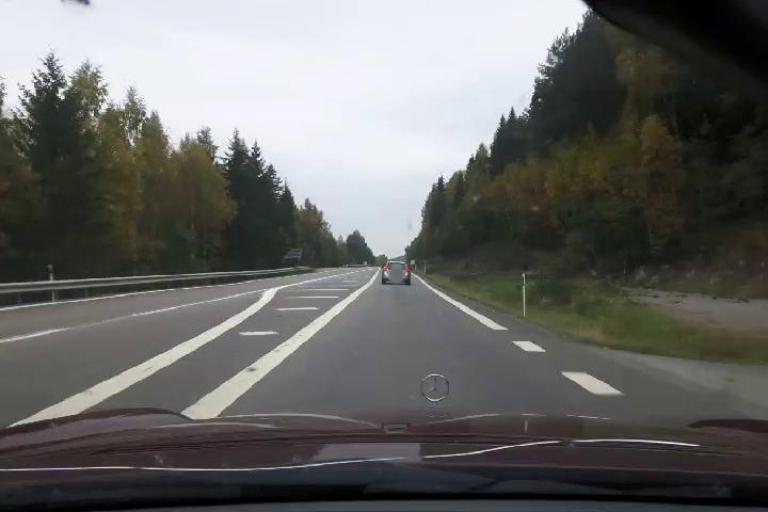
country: SE
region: Vaesternorrland
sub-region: Kramfors Kommun
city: Nordingra
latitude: 63.0403
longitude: 18.3265
